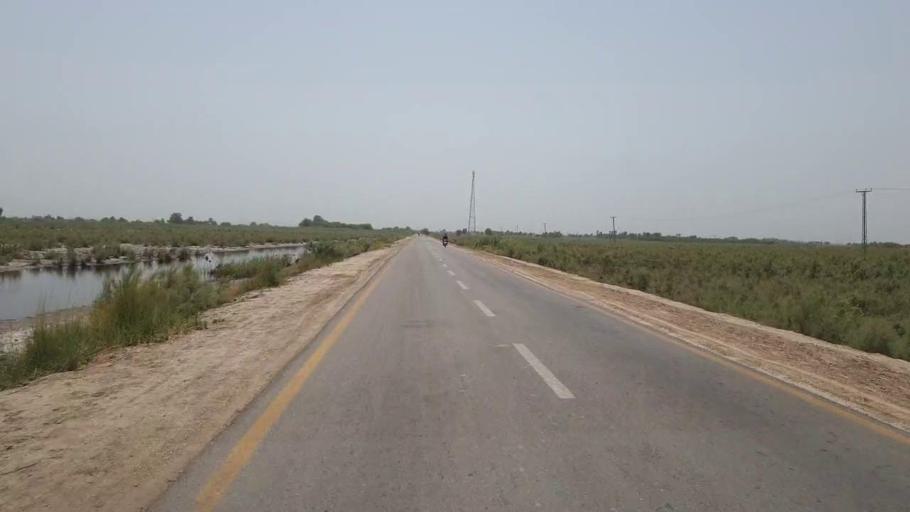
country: PK
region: Sindh
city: Moro
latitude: 26.6016
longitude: 68.0699
